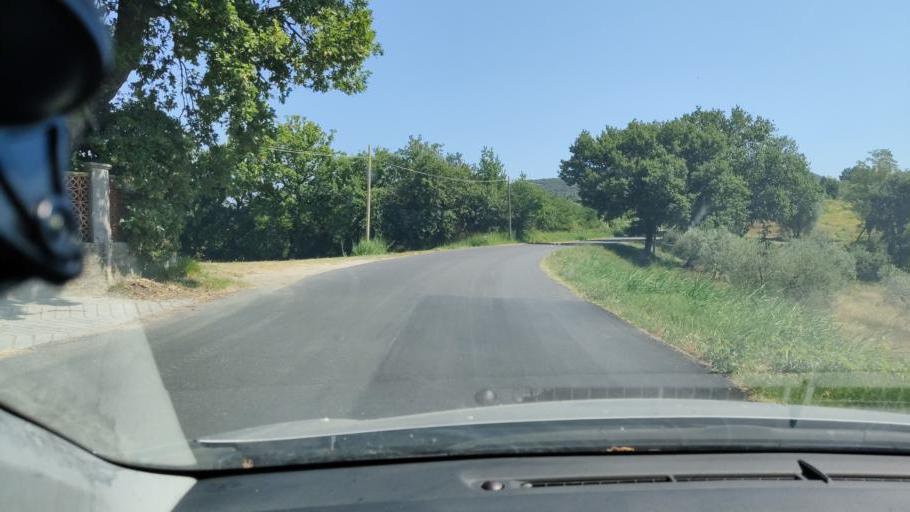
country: IT
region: Umbria
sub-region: Provincia di Terni
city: Fornole
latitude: 42.5346
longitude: 12.4511
